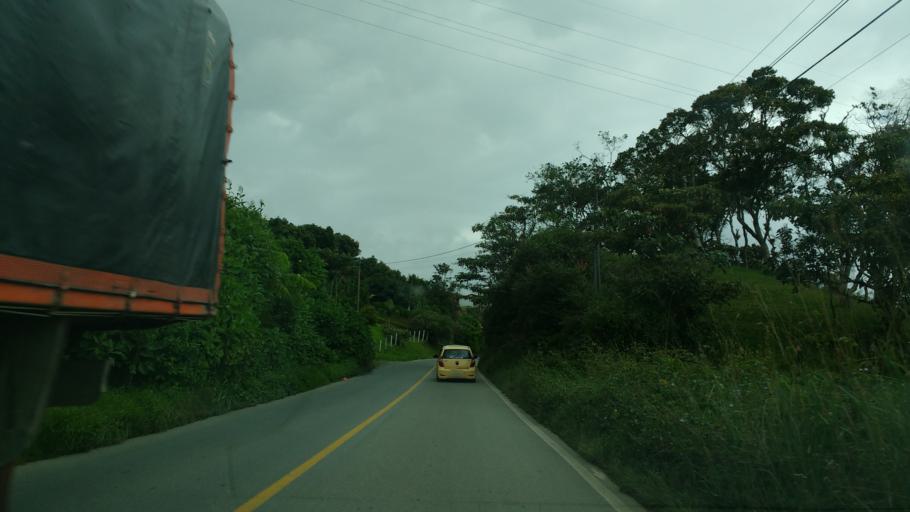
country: CO
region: Antioquia
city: Marinilla
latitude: 6.1837
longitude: -75.3015
